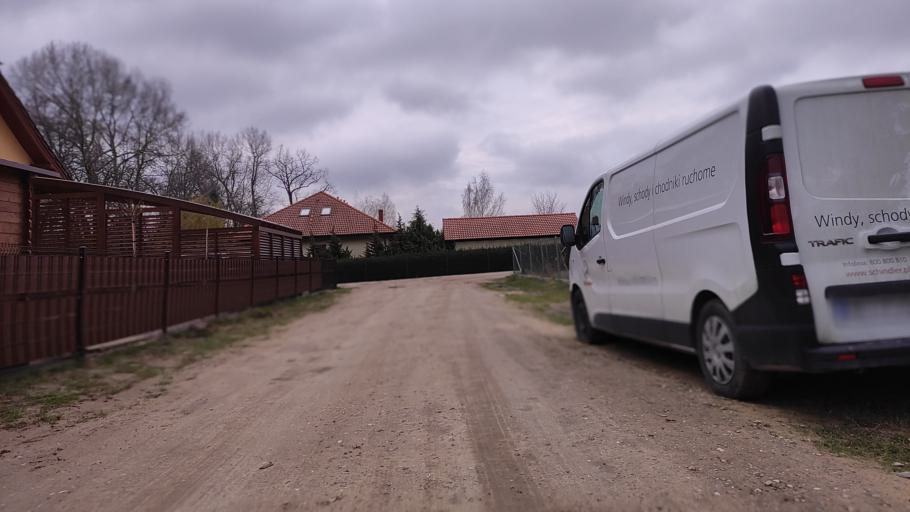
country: PL
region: Greater Poland Voivodeship
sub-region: Powiat poznanski
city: Kostrzyn
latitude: 52.4057
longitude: 17.1735
